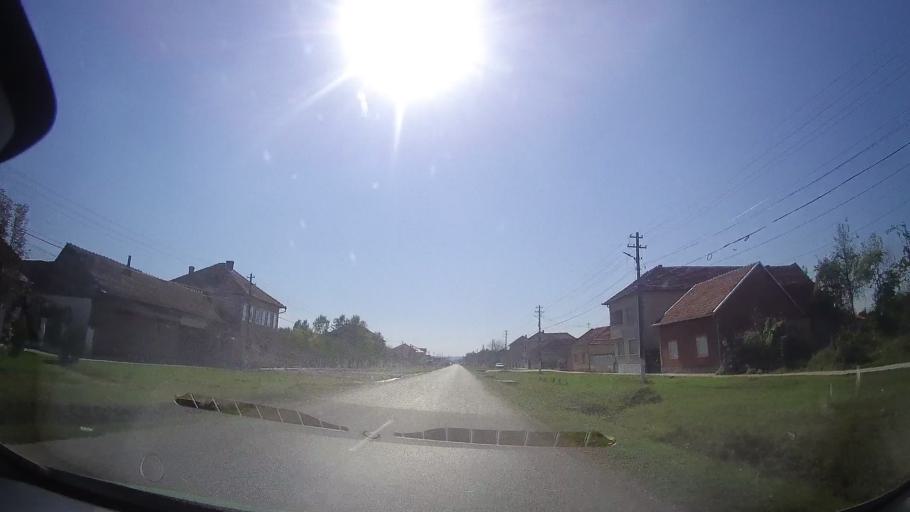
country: RO
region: Timis
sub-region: Comuna Bethausen
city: Bethausen
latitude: 45.8348
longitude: 21.9596
